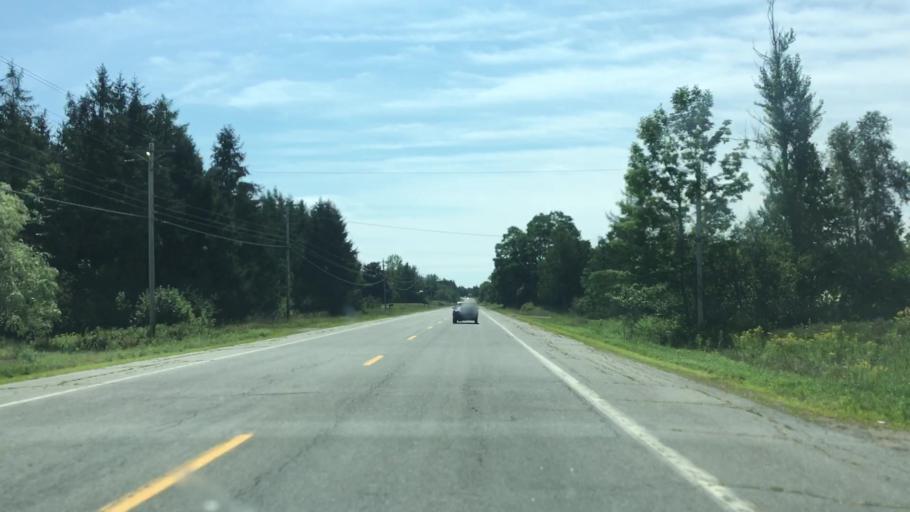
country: CA
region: New Brunswick
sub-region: Charlotte County
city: Saint Andrews
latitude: 45.1091
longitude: -67.1376
